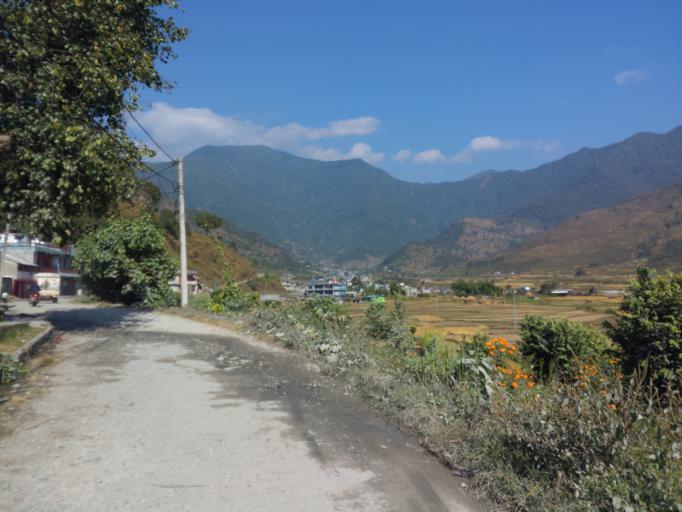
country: NP
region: Western Region
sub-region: Gandaki Zone
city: Pokhara
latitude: 28.2730
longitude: 83.9805
